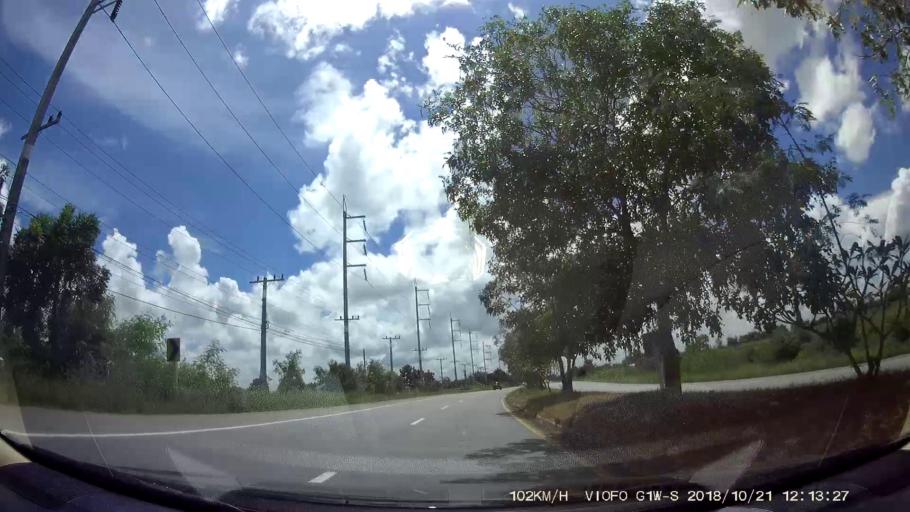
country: TH
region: Chaiyaphum
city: Chatturat
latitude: 15.3928
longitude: 101.8399
